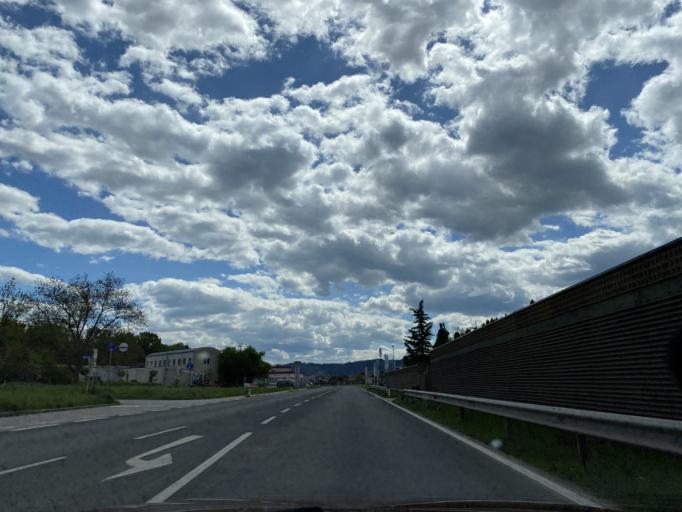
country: AT
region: Carinthia
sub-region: Politischer Bezirk Wolfsberg
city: Wolfsberg
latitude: 46.8124
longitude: 14.8332
